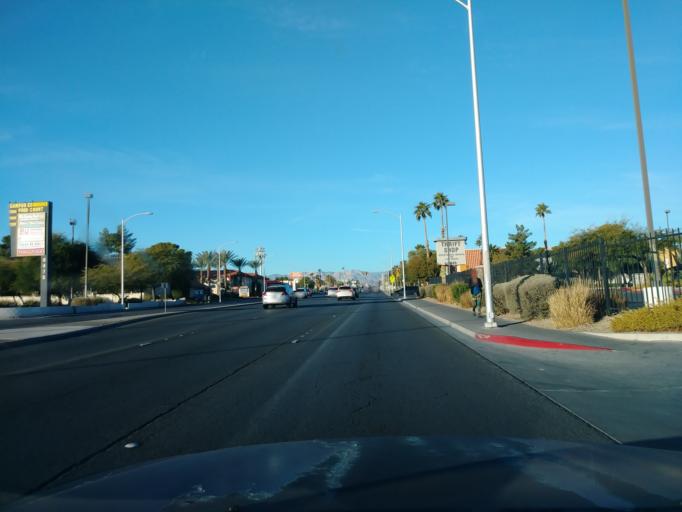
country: US
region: Nevada
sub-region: Clark County
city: Spring Valley
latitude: 36.1593
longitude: -115.2362
